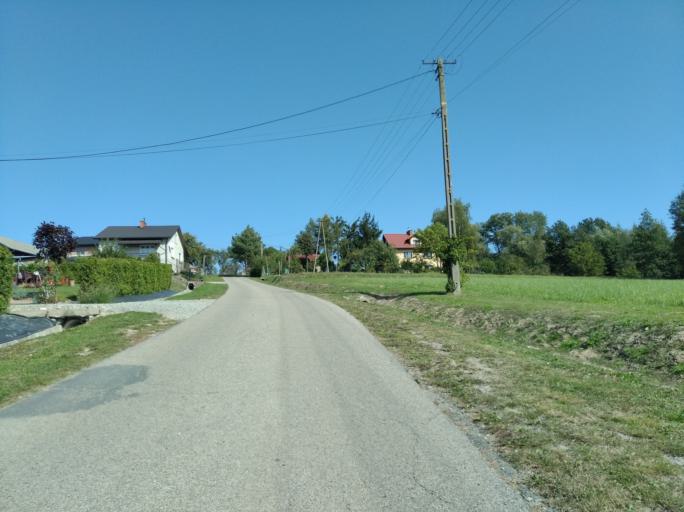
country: PL
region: Subcarpathian Voivodeship
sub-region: Powiat strzyzowski
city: Czudec
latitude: 49.9662
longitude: 21.8109
